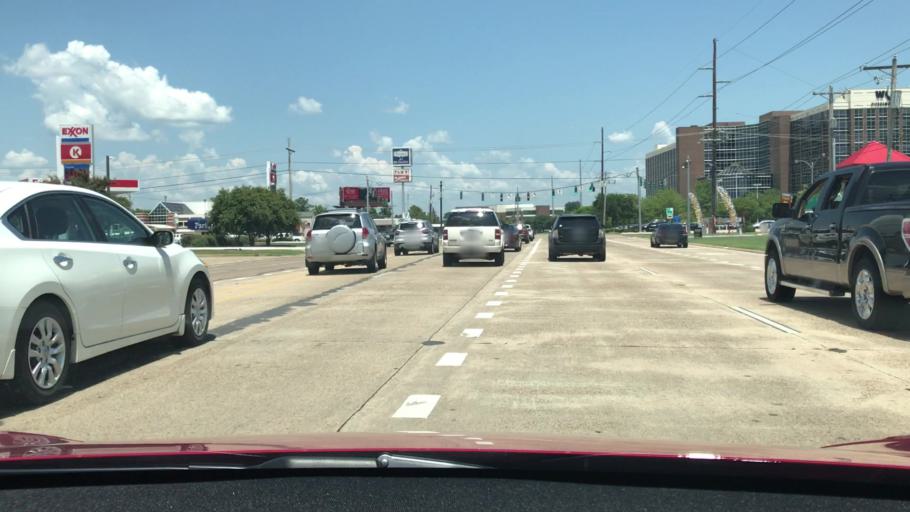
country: US
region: Louisiana
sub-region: Bossier Parish
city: Bossier City
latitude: 32.4313
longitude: -93.7131
